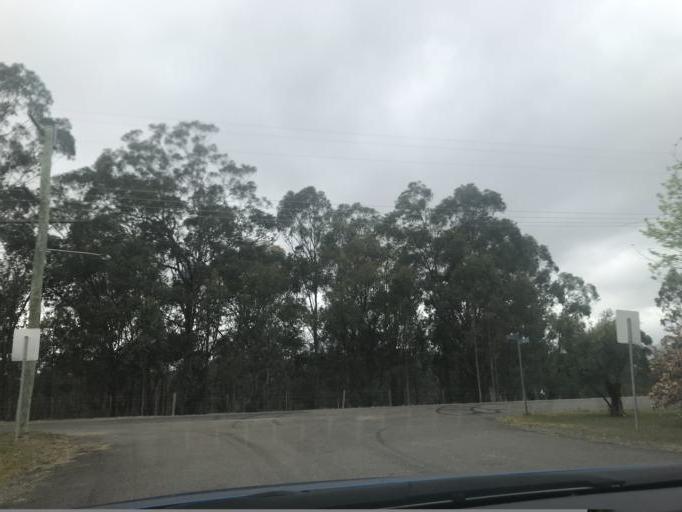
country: AU
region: New South Wales
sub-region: Cessnock
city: Cessnock
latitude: -32.9050
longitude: 151.2875
